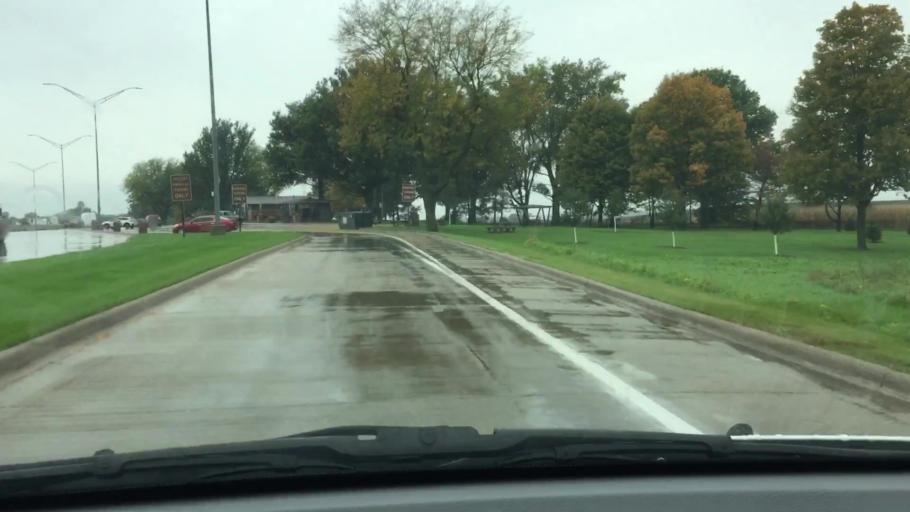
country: US
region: Iowa
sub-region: Iowa County
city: Marengo
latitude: 41.6963
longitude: -92.2303
